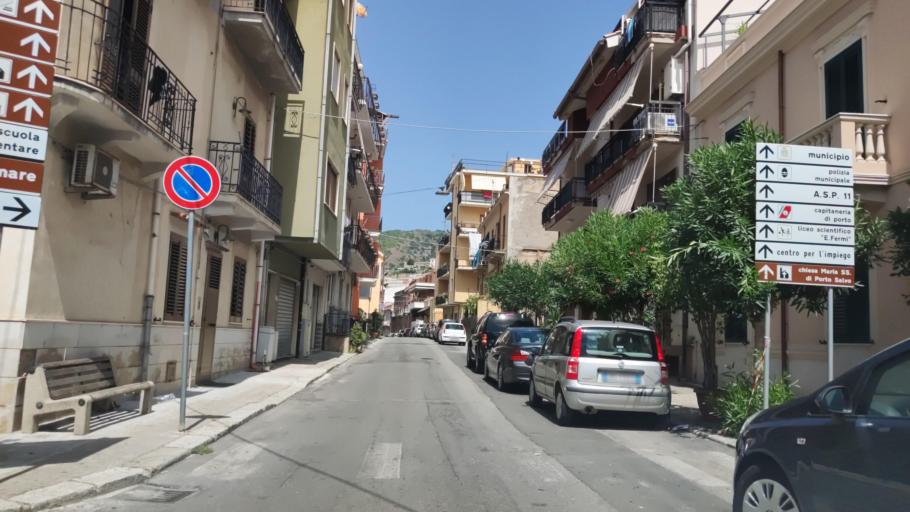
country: IT
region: Calabria
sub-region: Provincia di Reggio Calabria
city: Bagnara Calabra
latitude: 38.2837
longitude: 15.8002
